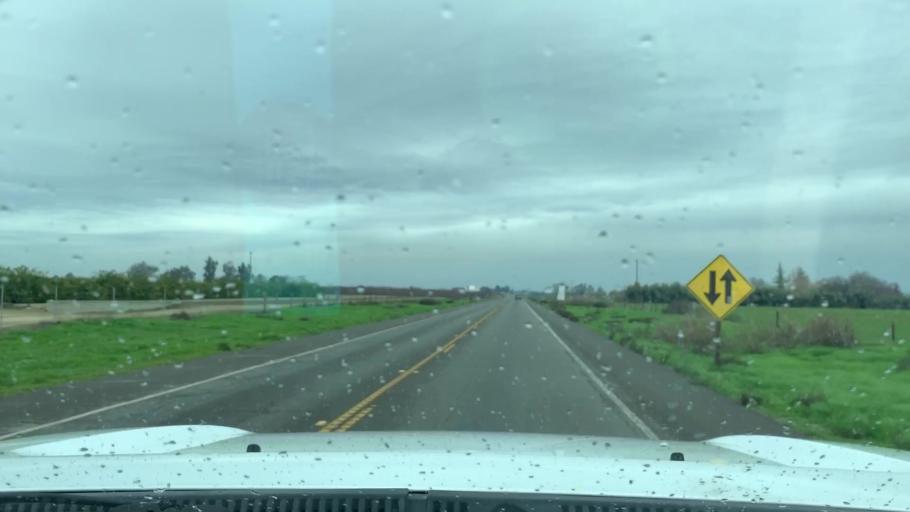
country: US
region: California
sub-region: Fresno County
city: Riverdale
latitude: 36.4110
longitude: -119.8053
